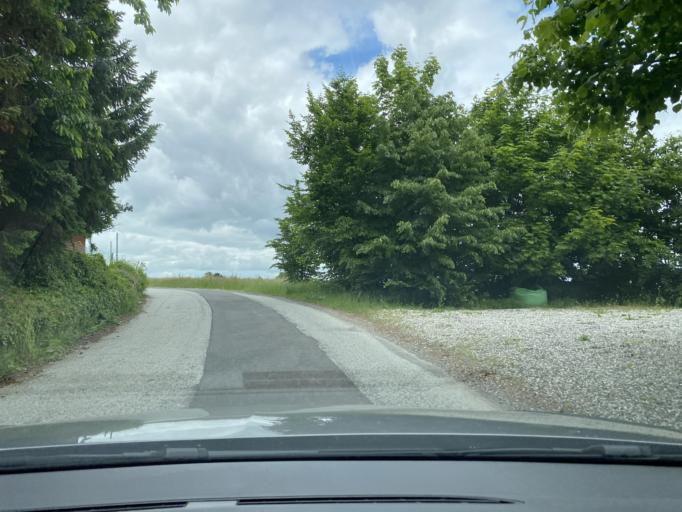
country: DK
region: South Denmark
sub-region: Vejle Kommune
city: Brejning
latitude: 55.6353
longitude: 9.7194
